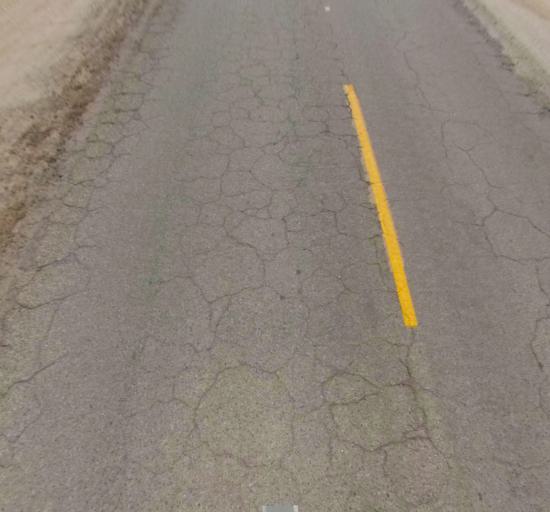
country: US
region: California
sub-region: Fresno County
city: Mendota
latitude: 36.8366
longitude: -120.2523
